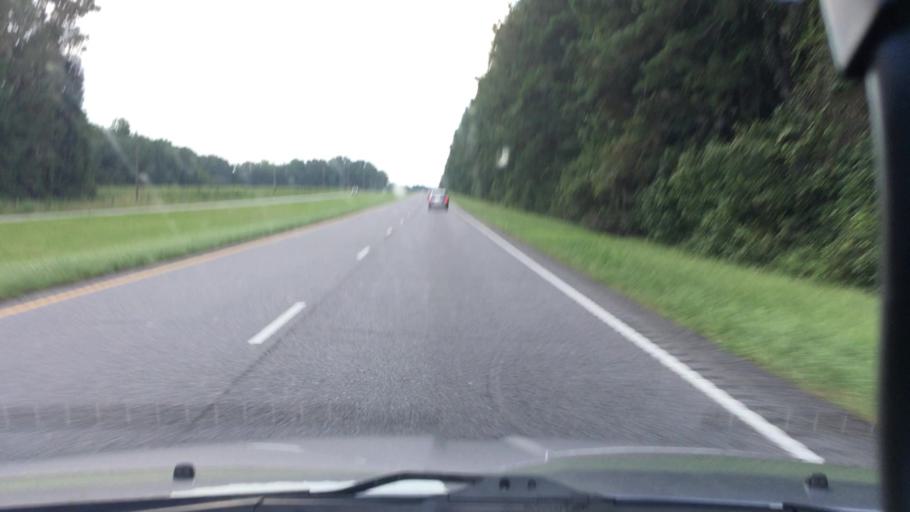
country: US
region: South Carolina
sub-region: Hampton County
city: Yemassee
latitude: 32.6167
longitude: -80.8177
